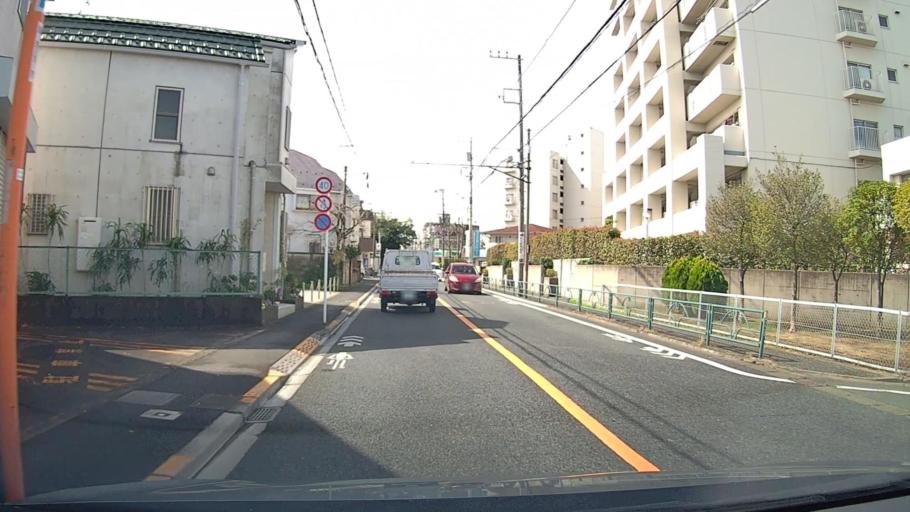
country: JP
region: Tokyo
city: Nishi-Tokyo-shi
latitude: 35.7345
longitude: 139.5508
